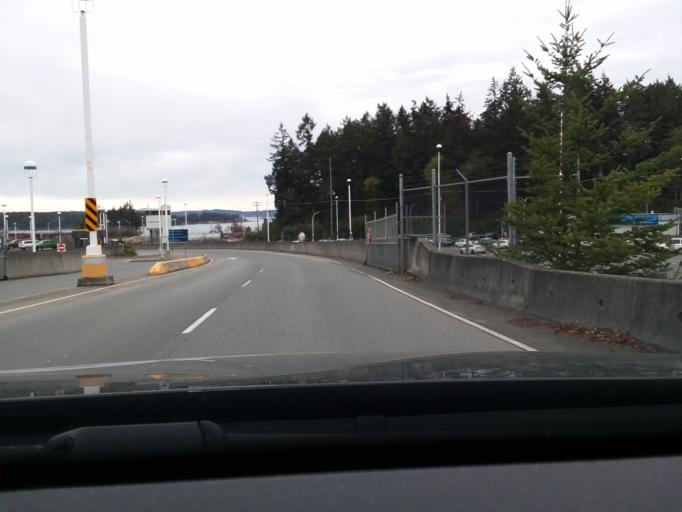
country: CA
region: British Columbia
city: North Saanich
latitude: 48.6847
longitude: -123.4115
